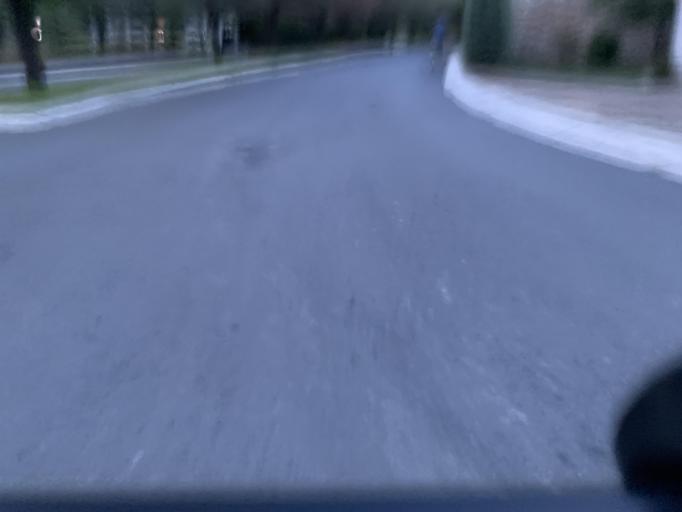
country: MX
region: Nuevo Leon
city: Santiago
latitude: 25.5059
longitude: -100.1850
